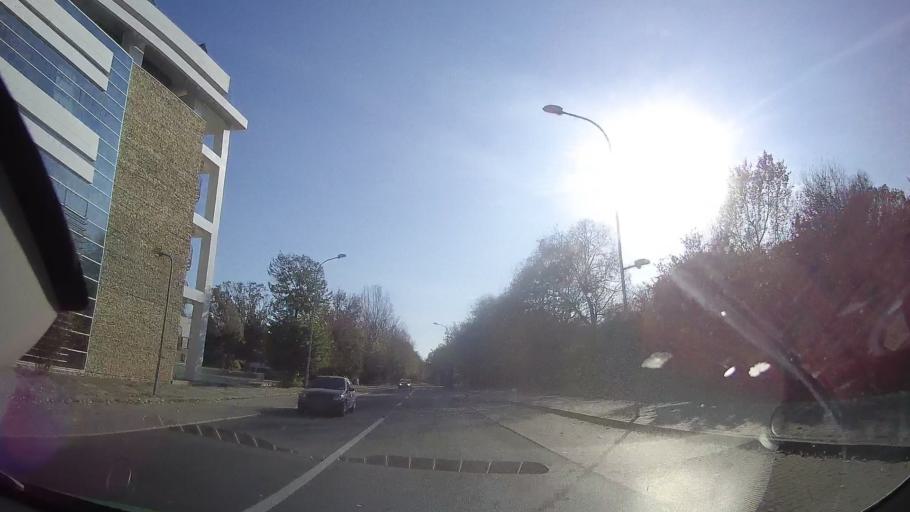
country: RO
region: Constanta
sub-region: Comuna Douazeci si Trei August
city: Douazeci si Trei August
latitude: 43.8787
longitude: 28.6030
